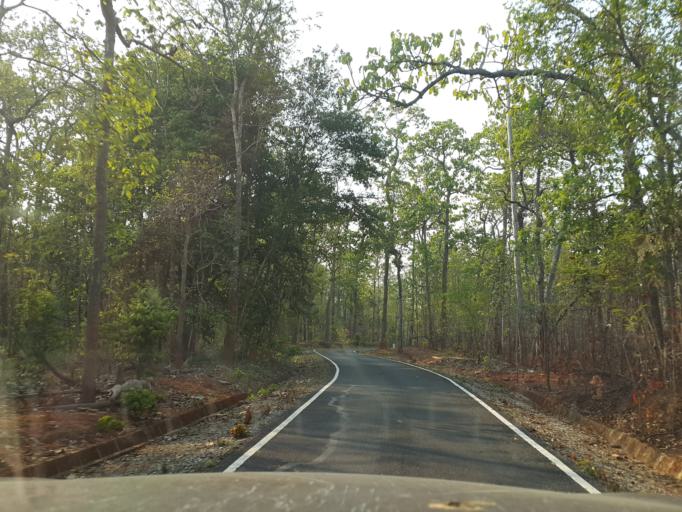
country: TH
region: Lamphun
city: Li
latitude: 17.6171
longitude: 98.8726
